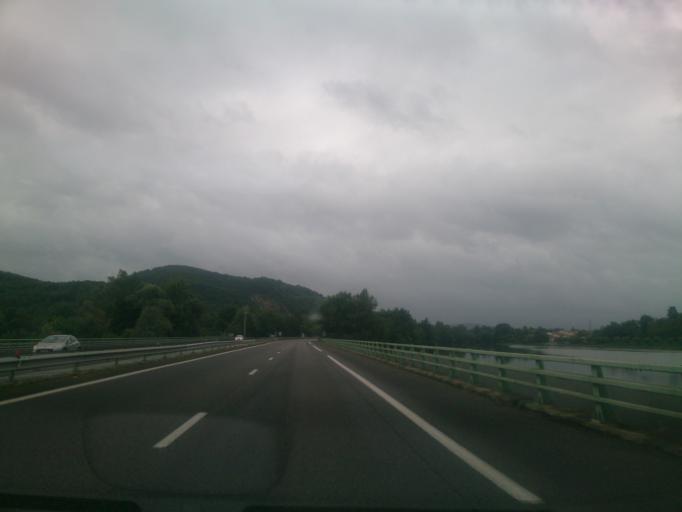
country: FR
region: Midi-Pyrenees
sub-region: Departement de la Haute-Garonne
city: Martres-Tolosane
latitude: 43.1814
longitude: 0.9793
